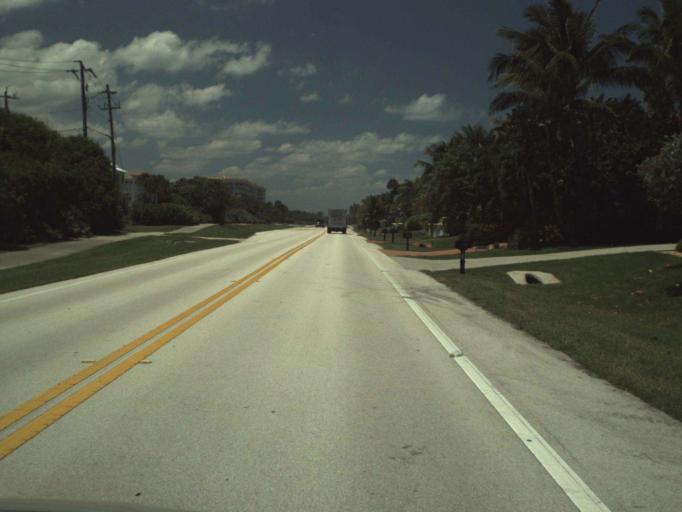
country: US
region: Florida
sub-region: Brevard County
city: Micco
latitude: 27.9198
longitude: -80.4815
